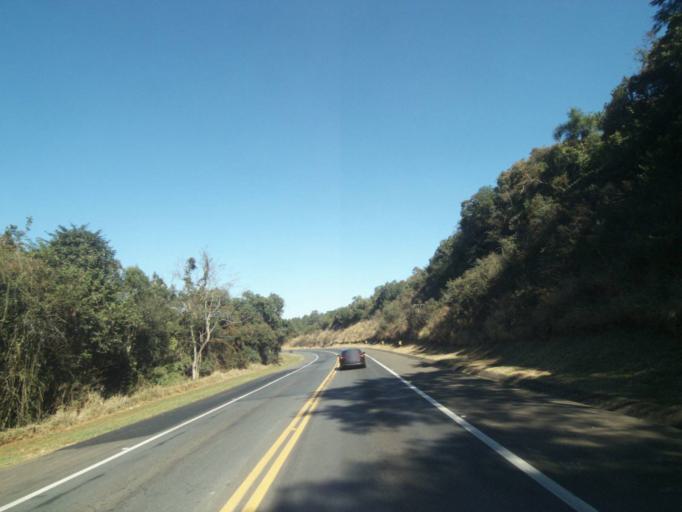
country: BR
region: Parana
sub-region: Tibagi
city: Tibagi
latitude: -24.7288
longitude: -50.5384
